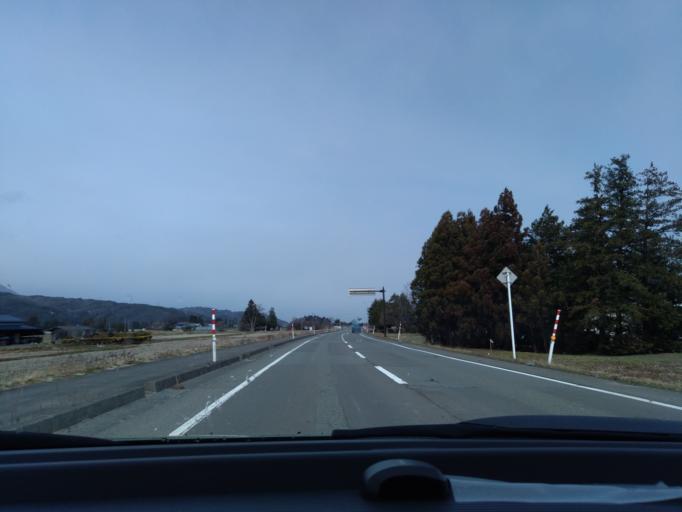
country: JP
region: Iwate
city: Morioka-shi
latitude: 39.5724
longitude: 141.1095
